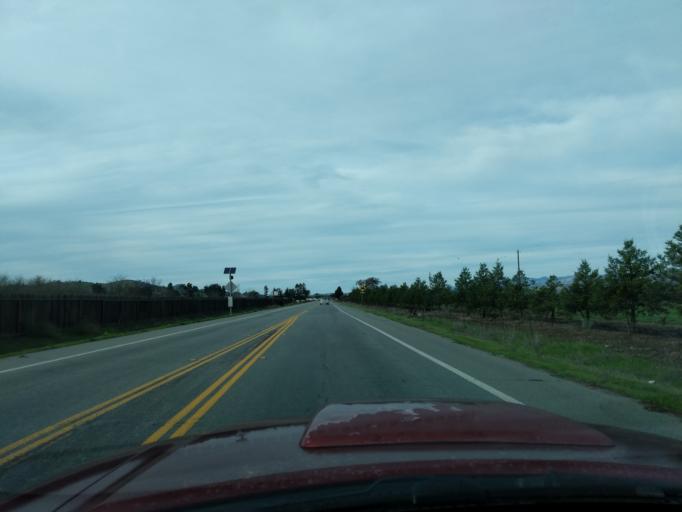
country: US
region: California
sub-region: Santa Clara County
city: San Martin
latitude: 37.0544
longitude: -121.6056
